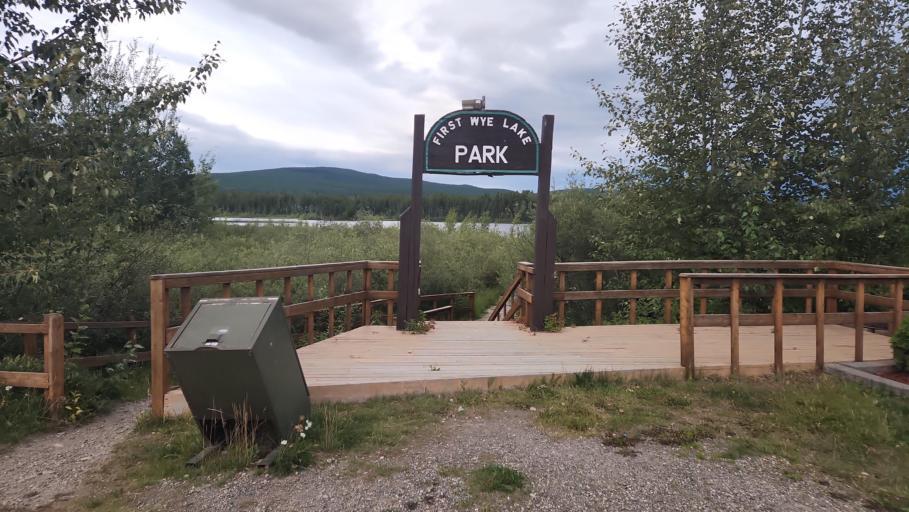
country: CA
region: Yukon
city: Watson Lake
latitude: 60.0635
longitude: -128.7058
